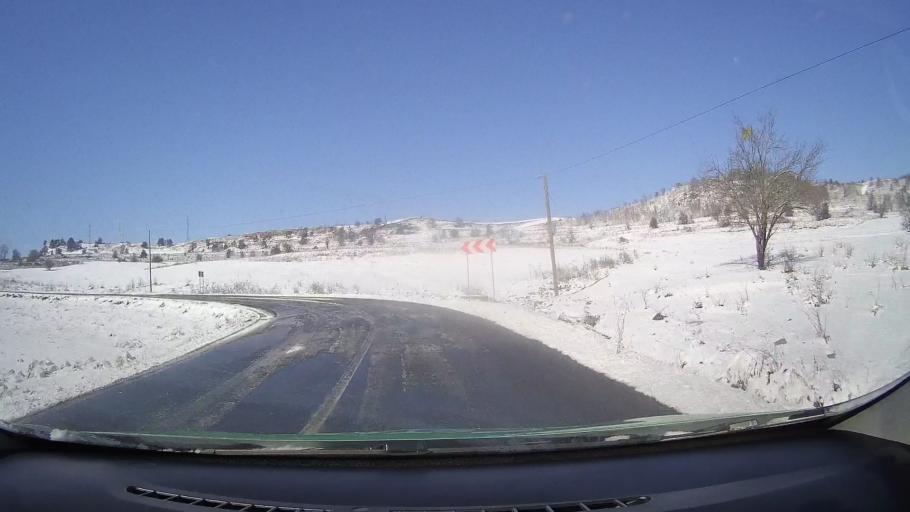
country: RO
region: Sibiu
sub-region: Comuna Avrig
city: Avrig
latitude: 45.7752
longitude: 24.3792
